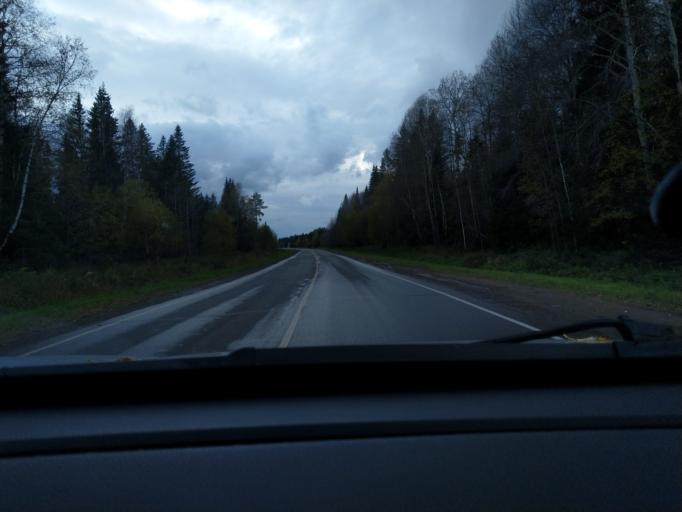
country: RU
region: Perm
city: Dobryanka
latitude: 58.4559
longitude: 56.4904
